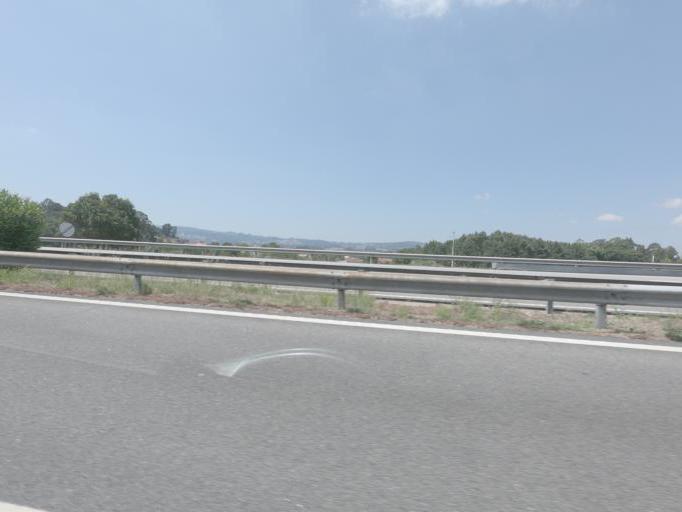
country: PT
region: Porto
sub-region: Penafiel
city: Penafiel
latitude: 41.2110
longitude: -8.2887
